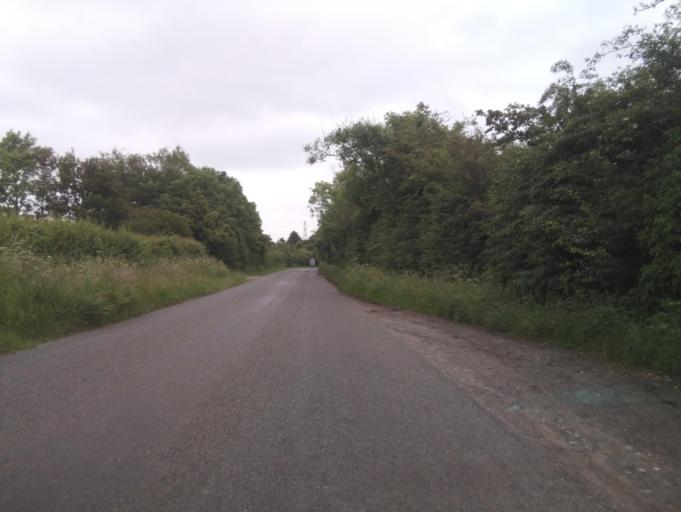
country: GB
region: England
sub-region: District of Rutland
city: Langham
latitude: 52.6705
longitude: -0.7544
